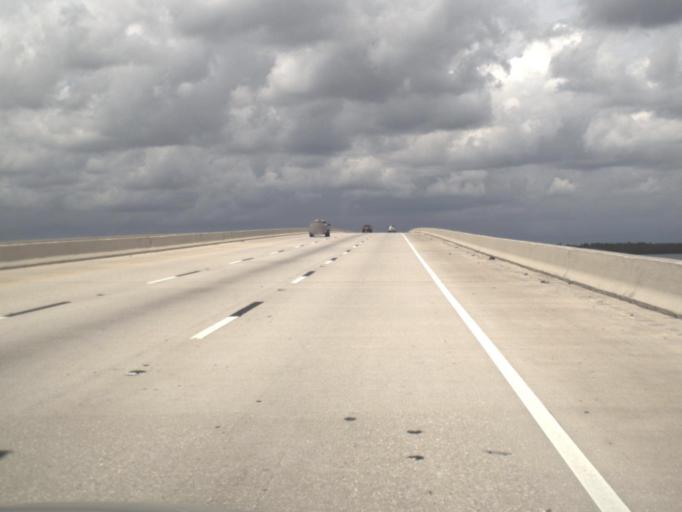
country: US
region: Florida
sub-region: Charlotte County
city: Punta Gorda
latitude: 26.9562
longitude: -82.0203
